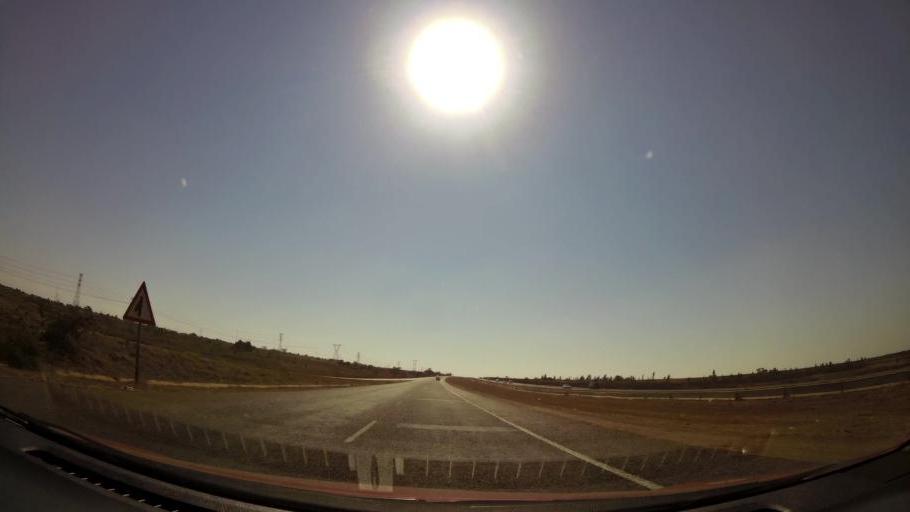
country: ZA
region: Gauteng
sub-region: City of Tshwane Metropolitan Municipality
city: Mabopane
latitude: -25.5541
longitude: 28.1086
